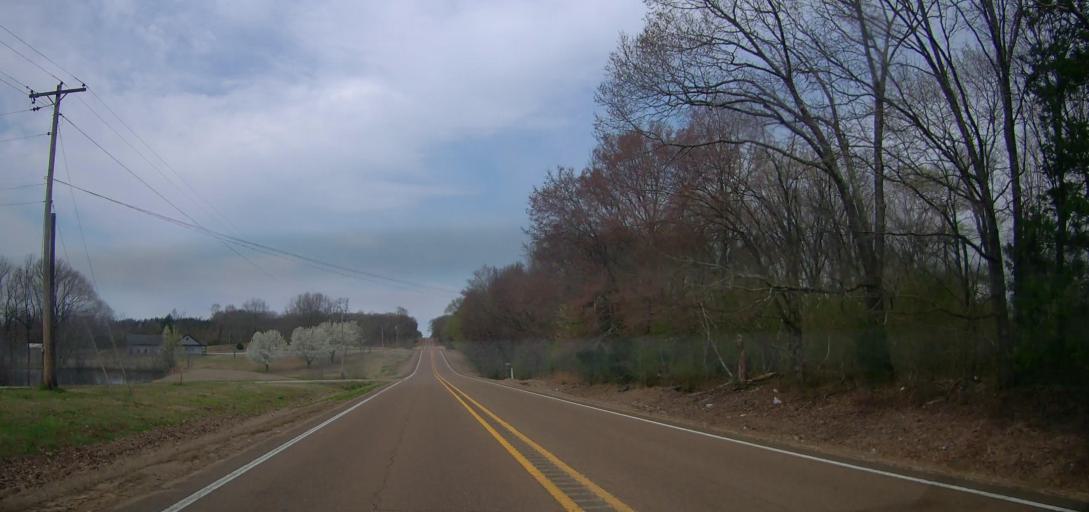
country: US
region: Mississippi
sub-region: Marshall County
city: Byhalia
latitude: 34.8330
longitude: -89.5791
